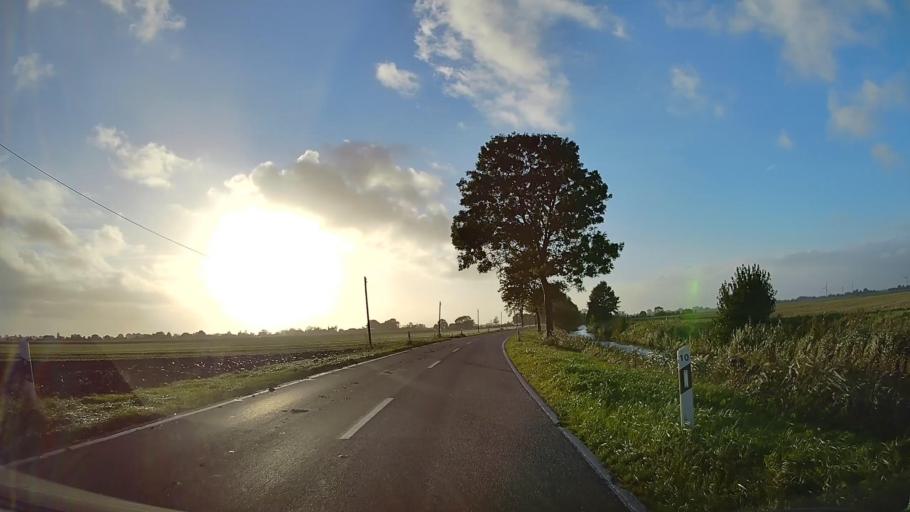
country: DE
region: Schleswig-Holstein
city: Suderau
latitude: 53.7935
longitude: 9.5082
